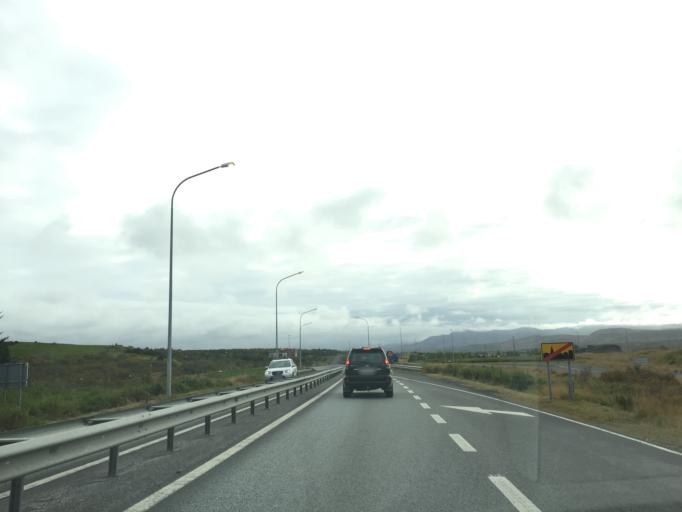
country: IS
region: Capital Region
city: Mosfellsbaer
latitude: 64.1025
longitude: -21.7631
